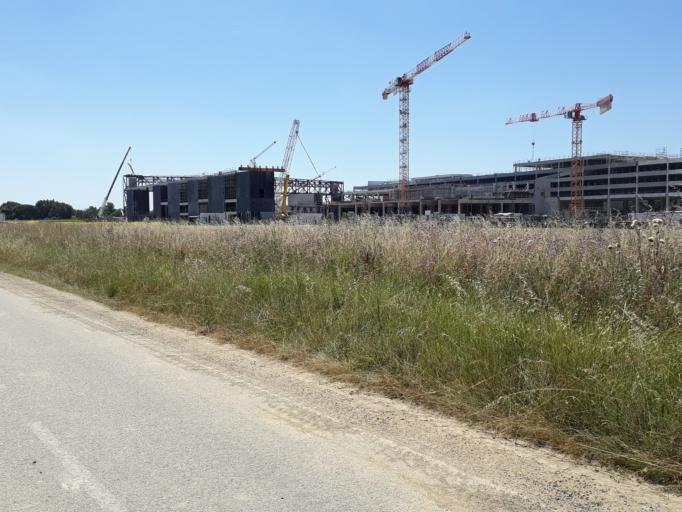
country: FR
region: Midi-Pyrenees
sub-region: Departement de la Haute-Garonne
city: Beauzelle
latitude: 43.6643
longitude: 1.3567
